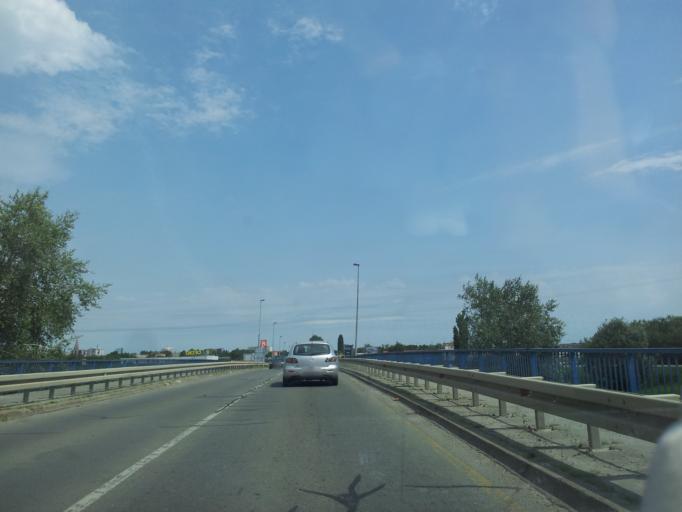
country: HR
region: Osjecko-Baranjska
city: Brijest
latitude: 45.5473
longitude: 18.6613
